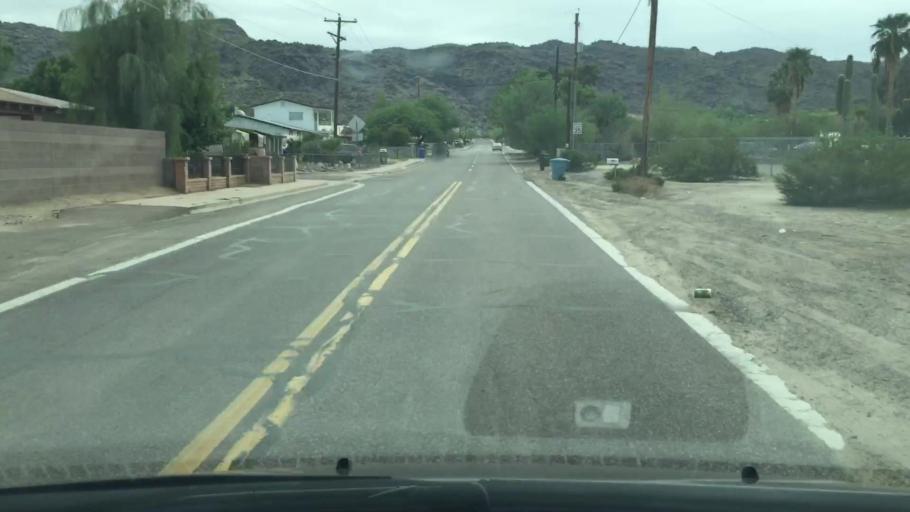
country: US
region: Arizona
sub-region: Maricopa County
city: Guadalupe
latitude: 33.3738
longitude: -112.0316
